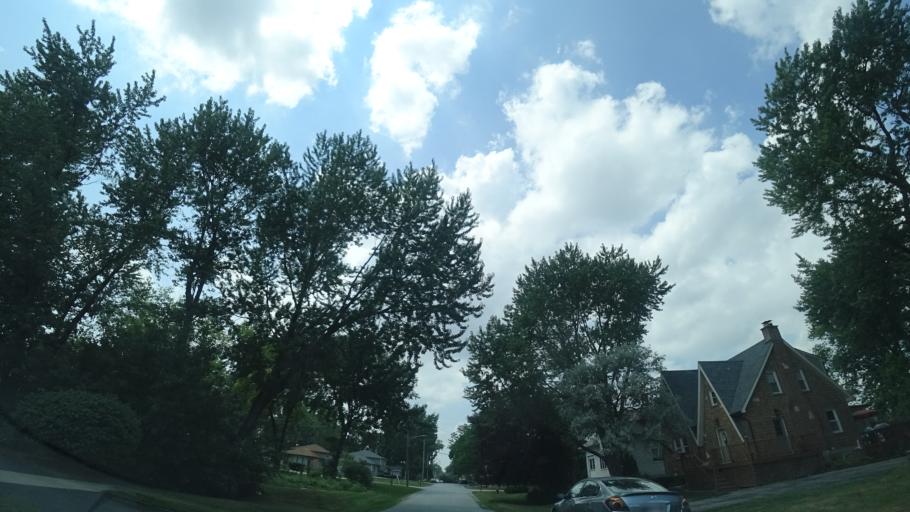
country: US
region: Illinois
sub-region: Cook County
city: Worth
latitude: 41.6919
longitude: -87.7922
